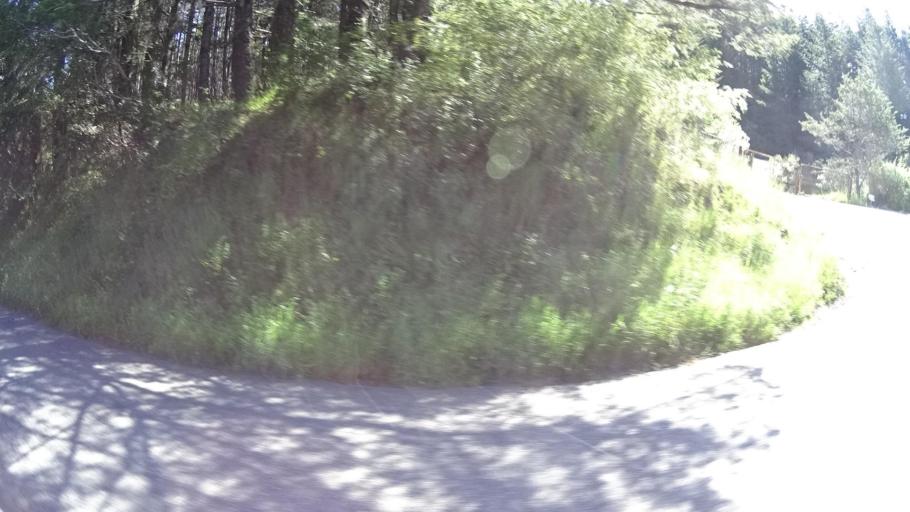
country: US
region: California
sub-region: Humboldt County
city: Rio Dell
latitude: 40.3009
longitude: -124.2505
